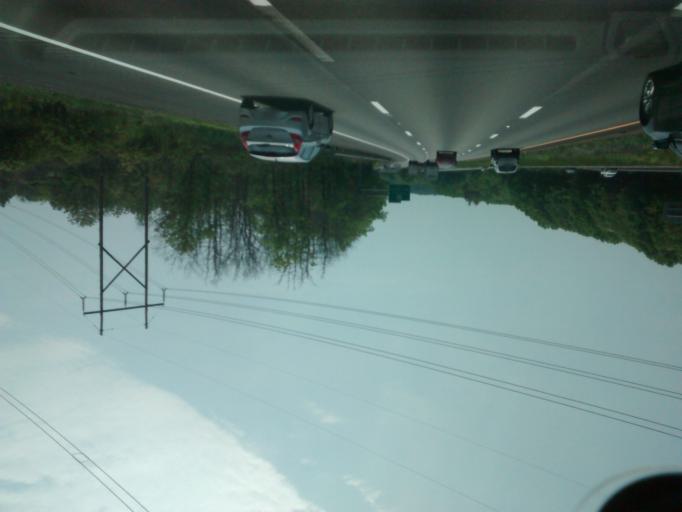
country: US
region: Massachusetts
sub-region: Norfolk County
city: Bellingham
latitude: 42.1028
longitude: -71.4461
